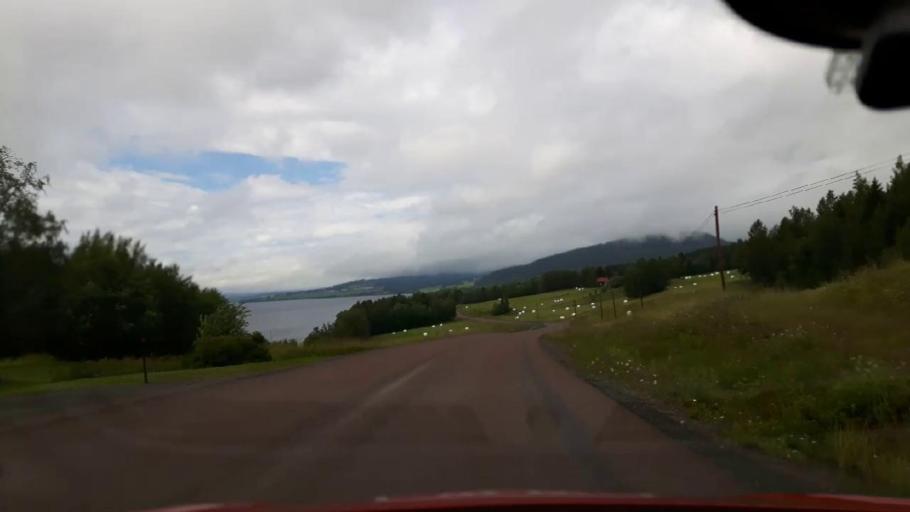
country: SE
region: Jaemtland
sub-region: Krokoms Kommun
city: Valla
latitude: 63.3672
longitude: 14.0500
